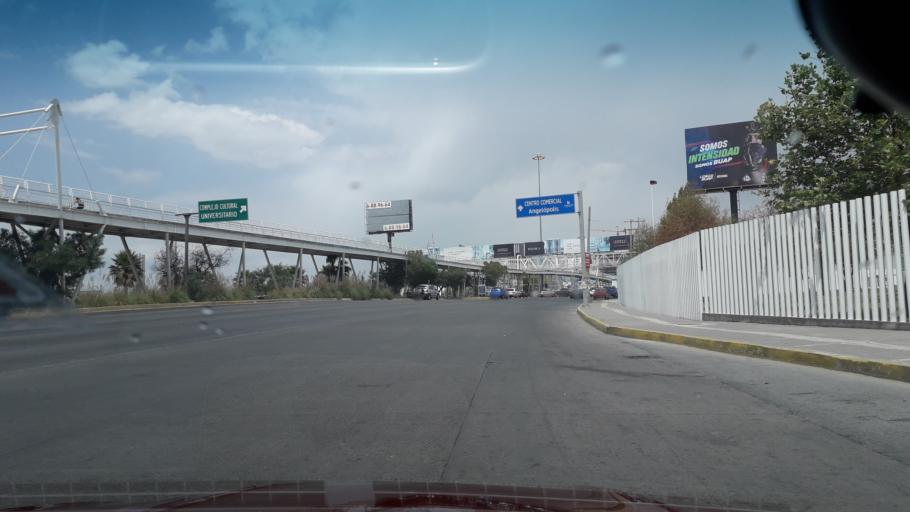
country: MX
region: Puebla
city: Tlazcalancingo
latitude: 19.0214
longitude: -98.2441
